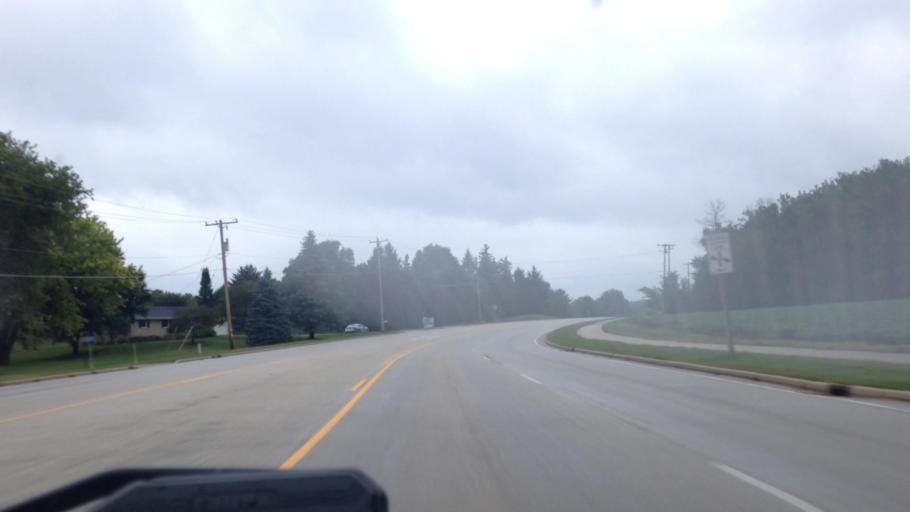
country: US
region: Wisconsin
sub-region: Waukesha County
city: Menomonee Falls
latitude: 43.1937
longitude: -88.1621
